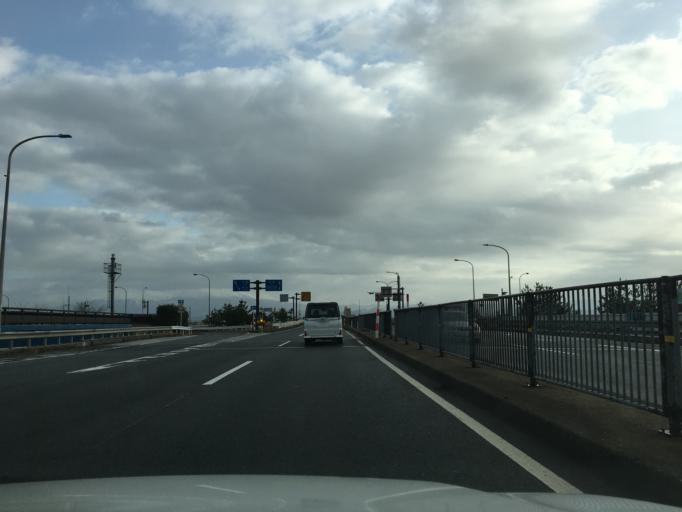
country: JP
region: Yamagata
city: Sakata
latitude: 38.8840
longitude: 139.8388
